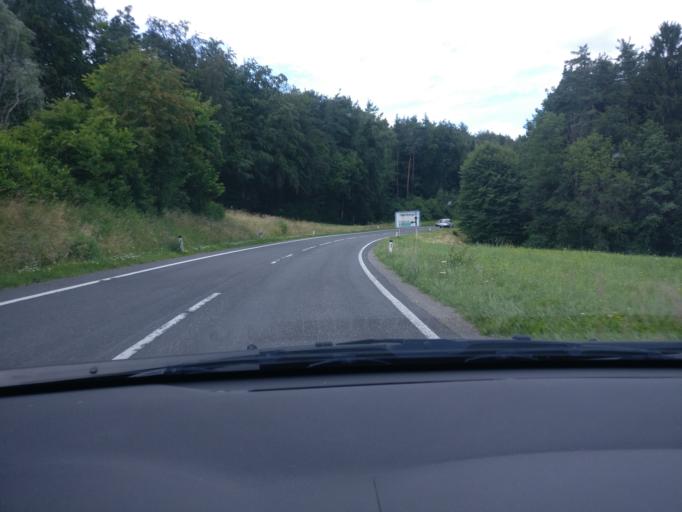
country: AT
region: Styria
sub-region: Politischer Bezirk Weiz
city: Nitscha
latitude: 47.1356
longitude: 15.7302
